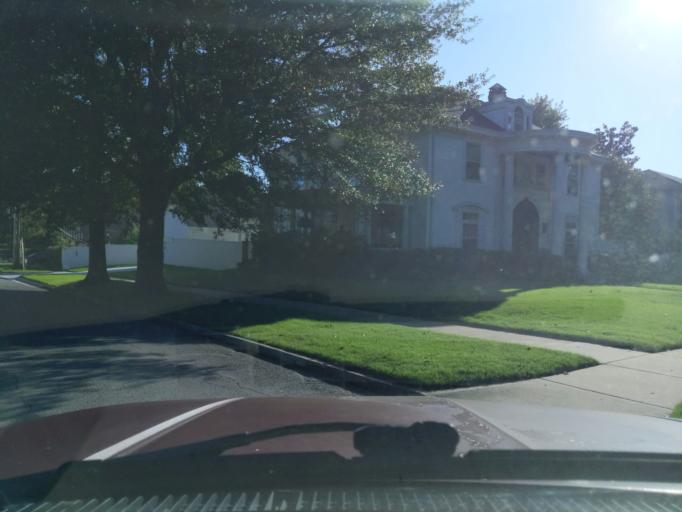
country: US
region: Oklahoma
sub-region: Tulsa County
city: Tulsa
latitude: 36.1342
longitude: -95.9818
